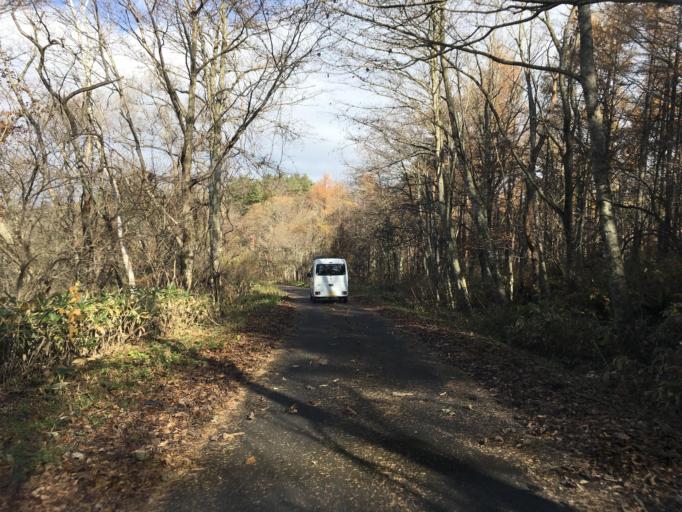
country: JP
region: Iwate
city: Mizusawa
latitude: 39.1265
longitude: 141.3031
